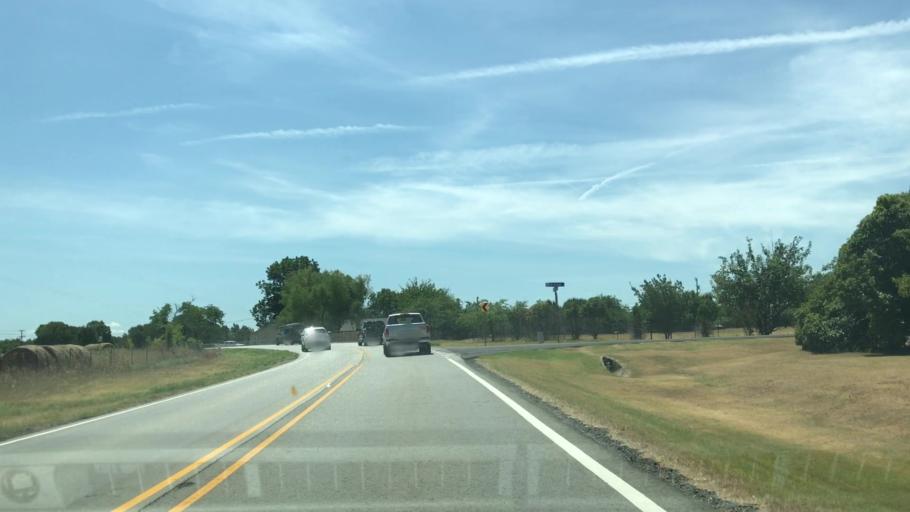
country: US
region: Texas
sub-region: Collin County
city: Lucas
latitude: 33.1066
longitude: -96.5966
